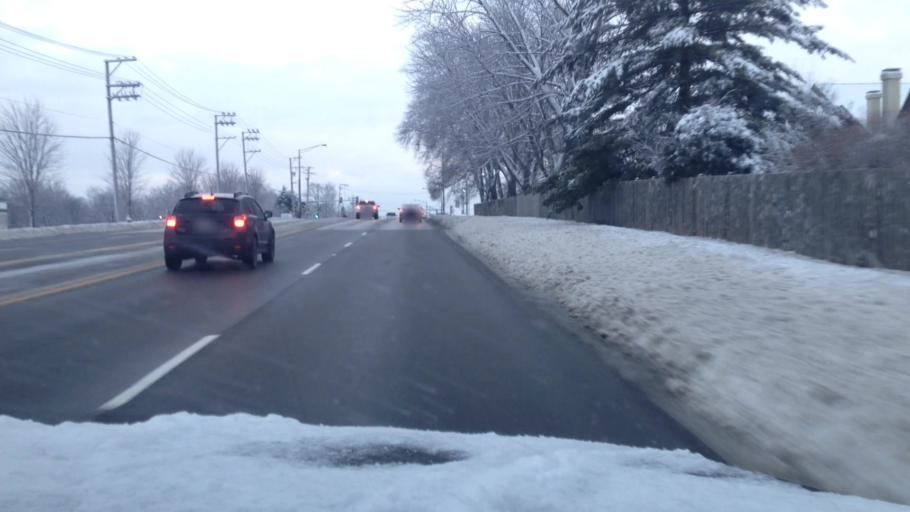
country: US
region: Illinois
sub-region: Kane County
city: South Elgin
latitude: 42.0091
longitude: -88.3150
